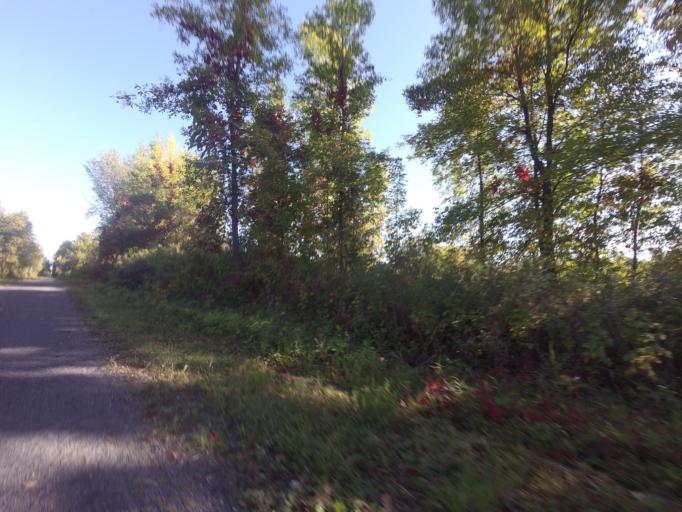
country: CA
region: Ontario
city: Hawkesbury
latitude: 45.5254
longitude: -74.5491
